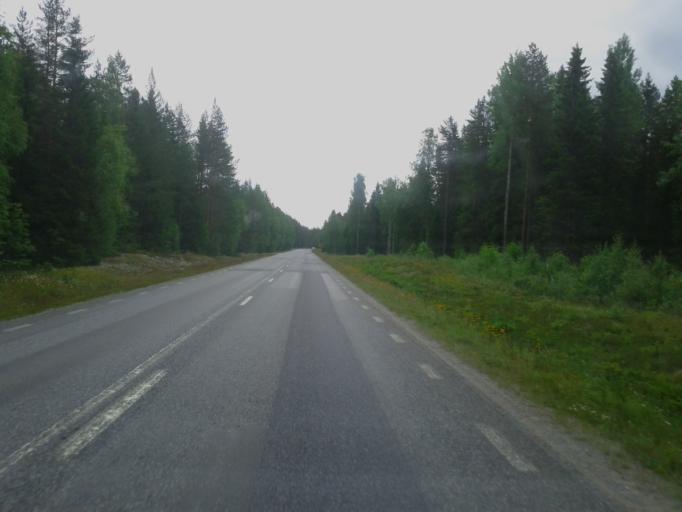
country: SE
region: Vaesternorrland
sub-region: OErnskoeldsviks Kommun
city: Bjasta
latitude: 63.2270
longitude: 18.4545
